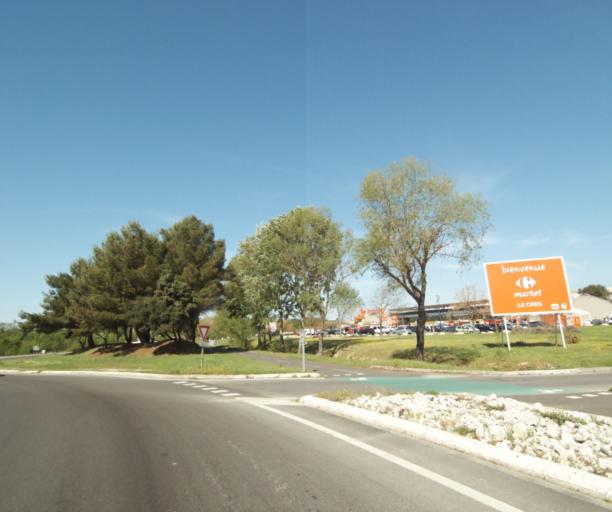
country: FR
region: Languedoc-Roussillon
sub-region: Departement de l'Herault
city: Le Cres
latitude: 43.6591
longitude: 3.9357
